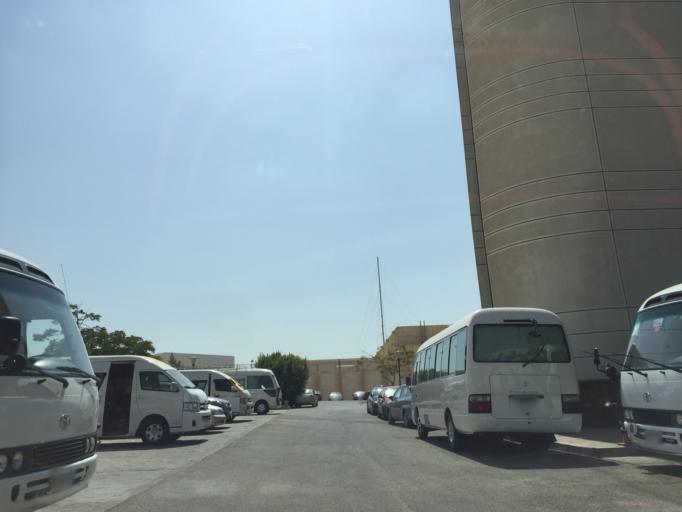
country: EG
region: Al Jizah
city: Awsim
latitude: 30.0709
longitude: 31.0218
